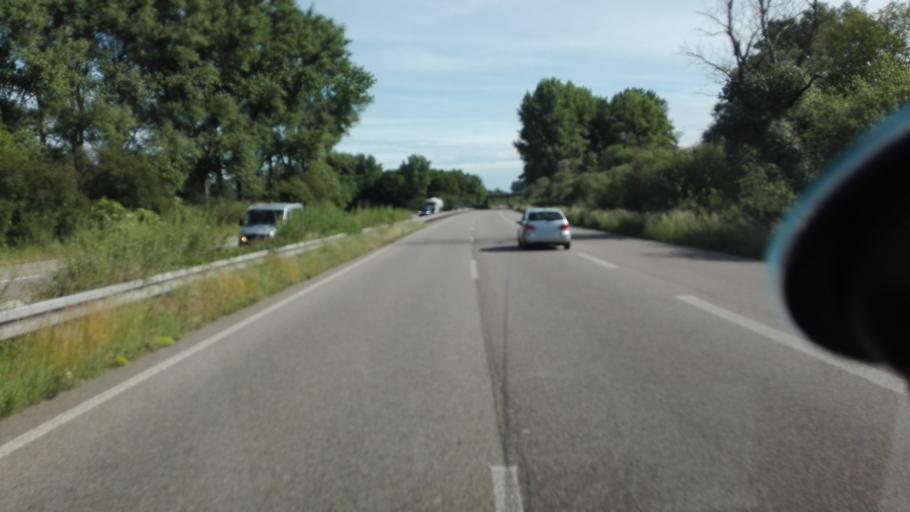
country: DE
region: Baden-Wuerttemberg
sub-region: Karlsruhe Region
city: Eggenstein-Leopoldshafen
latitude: 49.0511
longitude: 8.3672
